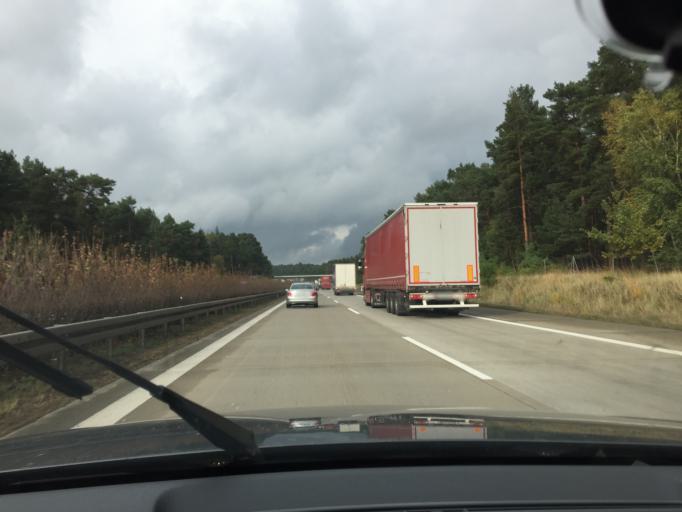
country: DE
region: Brandenburg
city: Schwerin
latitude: 52.1913
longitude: 13.6158
